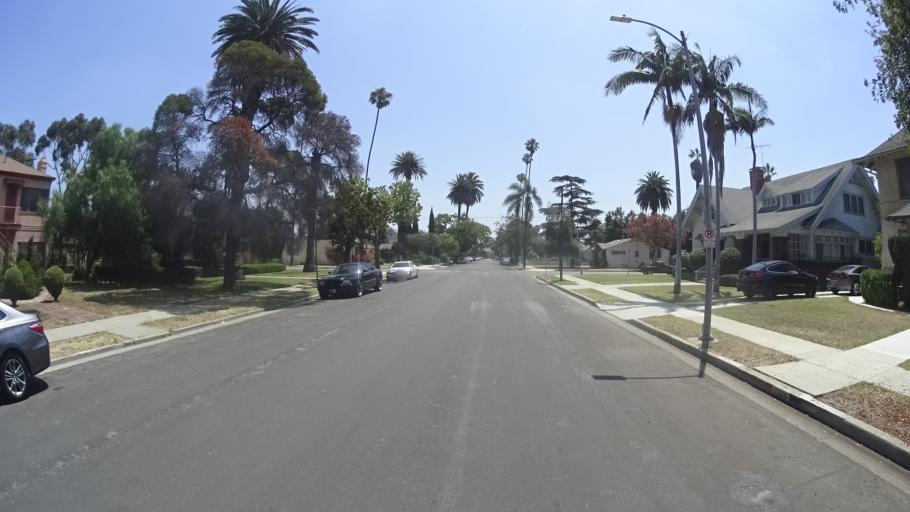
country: US
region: California
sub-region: Los Angeles County
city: View Park-Windsor Hills
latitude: 34.0360
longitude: -118.3160
